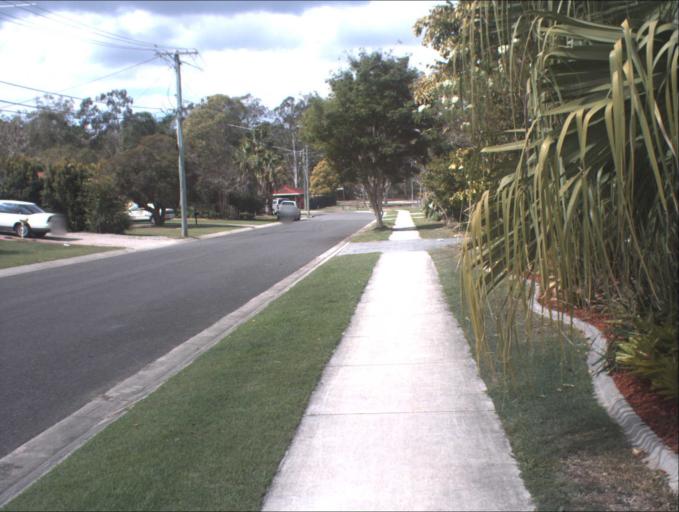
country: AU
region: Queensland
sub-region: Brisbane
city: Sunnybank Hills
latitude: -27.6677
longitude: 153.0490
